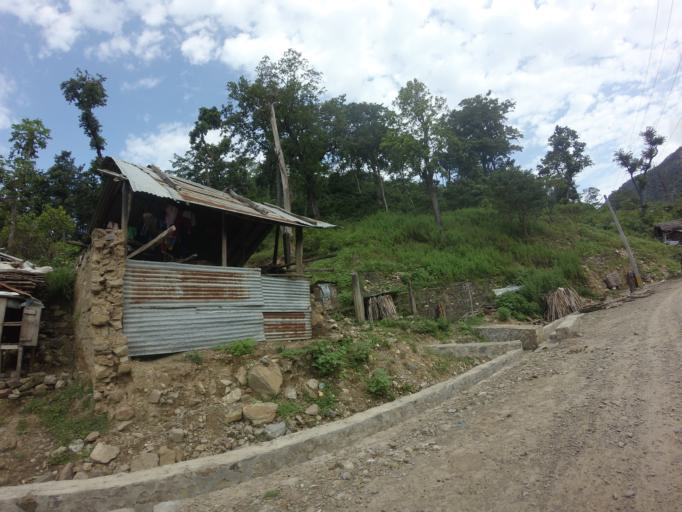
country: NP
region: Far Western
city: Tikapur
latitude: 28.6483
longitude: 81.2854
